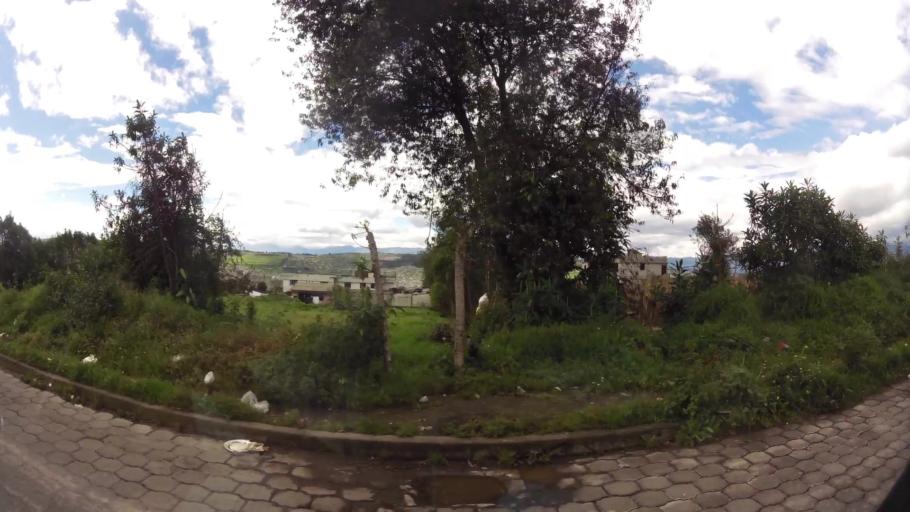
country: EC
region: Pichincha
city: Sangolqui
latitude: -0.3356
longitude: -78.5555
